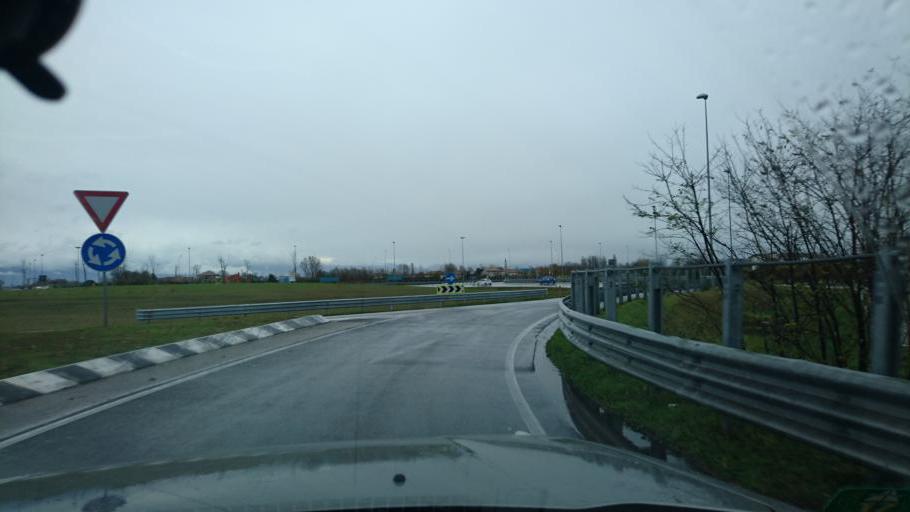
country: IT
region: Veneto
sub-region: Provincia di Treviso
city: Castelfranco Veneto
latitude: 45.6507
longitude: 11.9273
